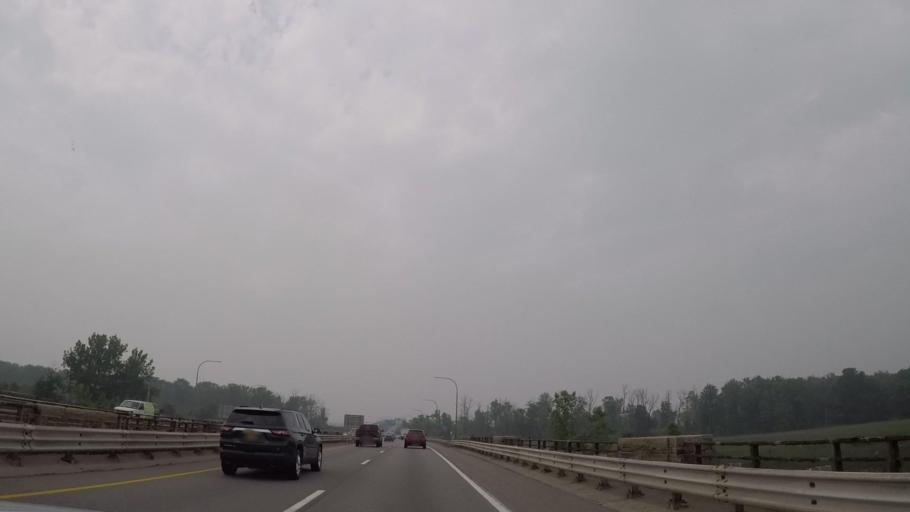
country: US
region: New York
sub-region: Erie County
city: Grandyle Village
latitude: 43.0592
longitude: -78.9904
